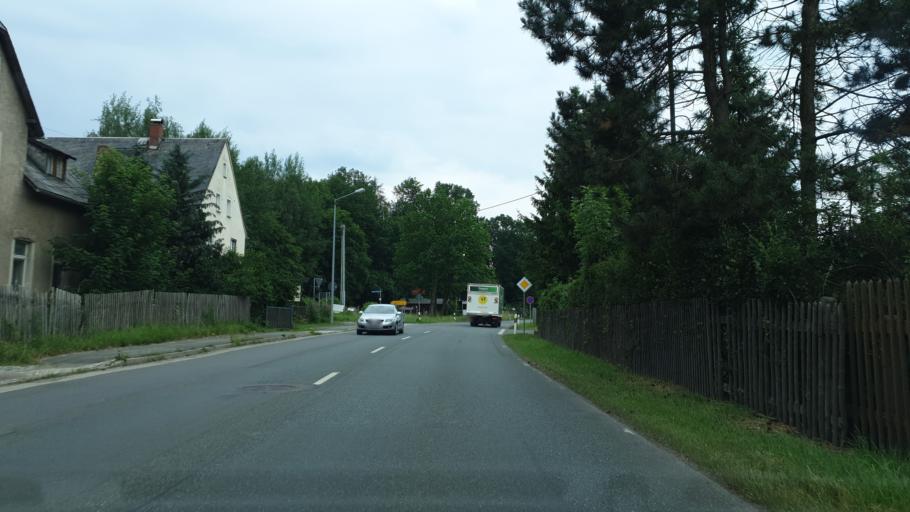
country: DE
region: Saxony
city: Lengenfeld
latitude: 50.5655
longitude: 12.3829
